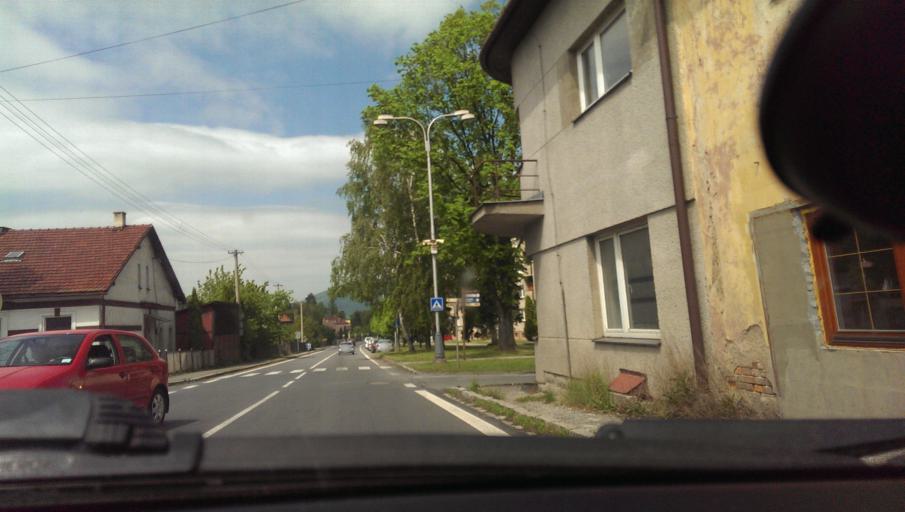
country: CZ
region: Moravskoslezsky
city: Frenstat pod Radhostem
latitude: 49.5484
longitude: 18.2071
